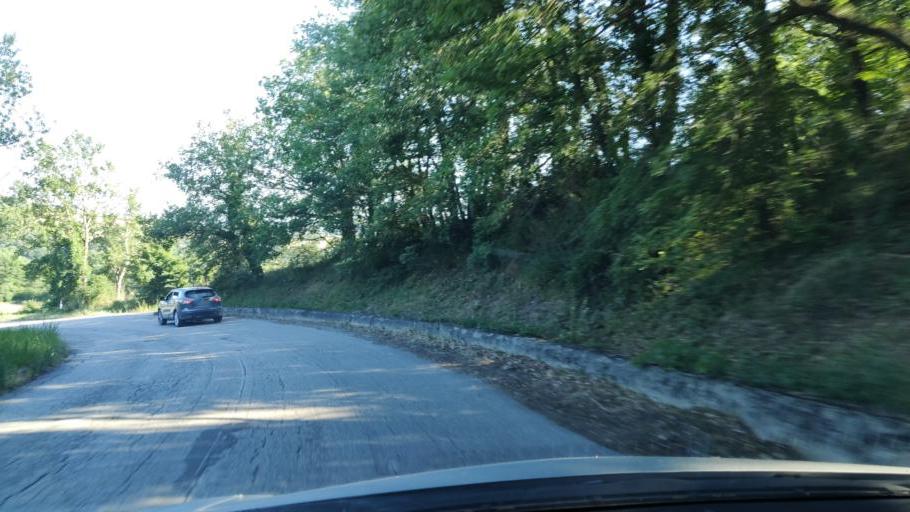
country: IT
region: Umbria
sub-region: Provincia di Terni
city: Penna in Teverina
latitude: 42.4840
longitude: 12.3673
